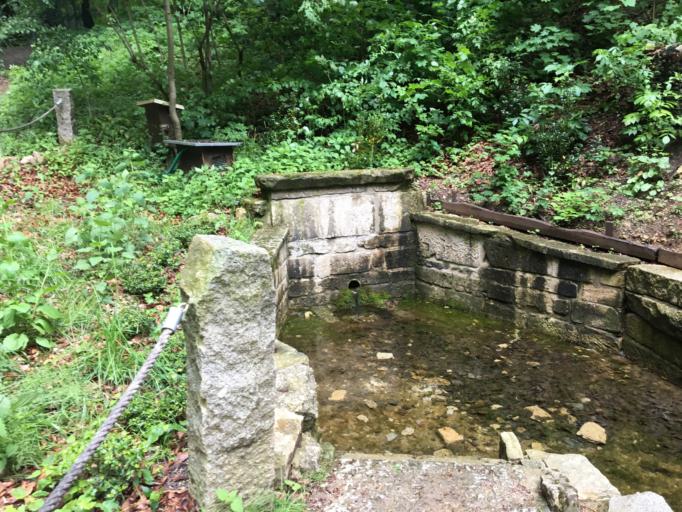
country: DE
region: Thuringia
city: Worbis
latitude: 51.4277
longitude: 10.3451
